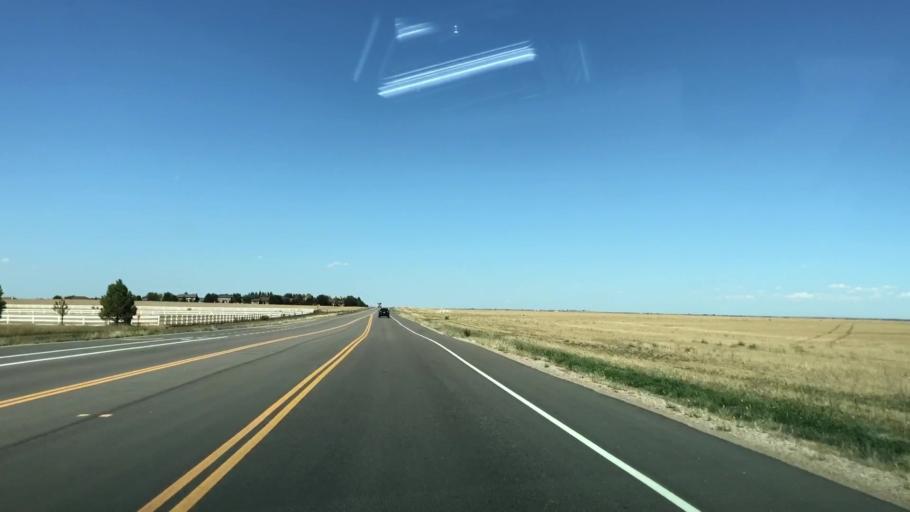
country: US
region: Colorado
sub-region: Weld County
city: Windsor
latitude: 40.4550
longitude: -104.9441
